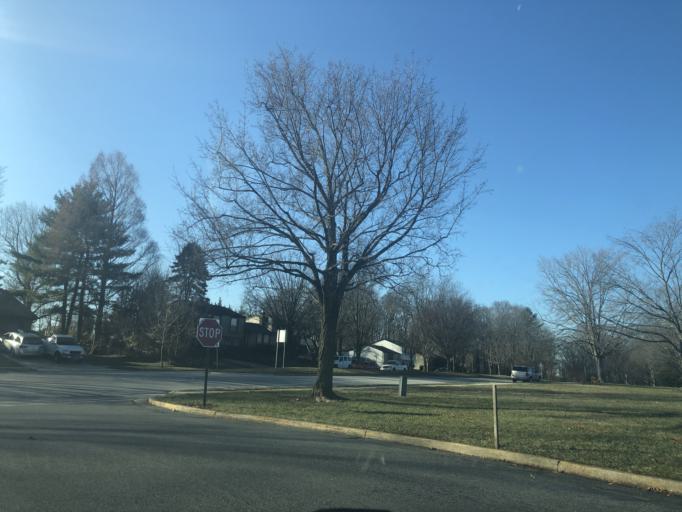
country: US
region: Maryland
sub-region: Howard County
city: Columbia
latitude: 39.2067
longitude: -76.8439
